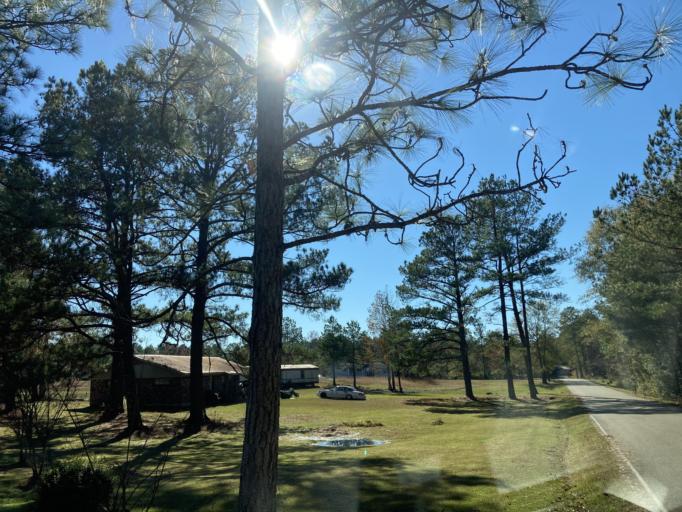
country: US
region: Mississippi
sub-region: Lamar County
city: Sumrall
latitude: 31.2919
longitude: -89.6487
